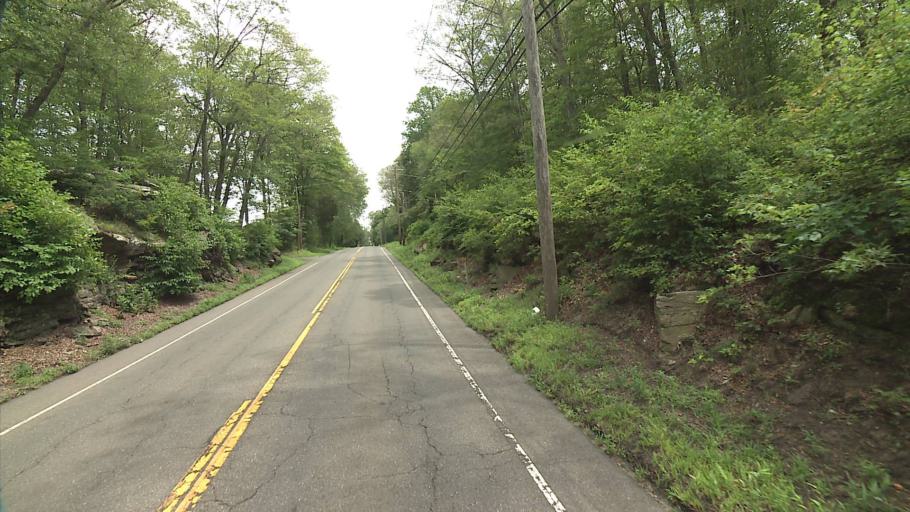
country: US
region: Connecticut
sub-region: Middlesex County
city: Chester Center
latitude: 41.3587
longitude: -72.5065
